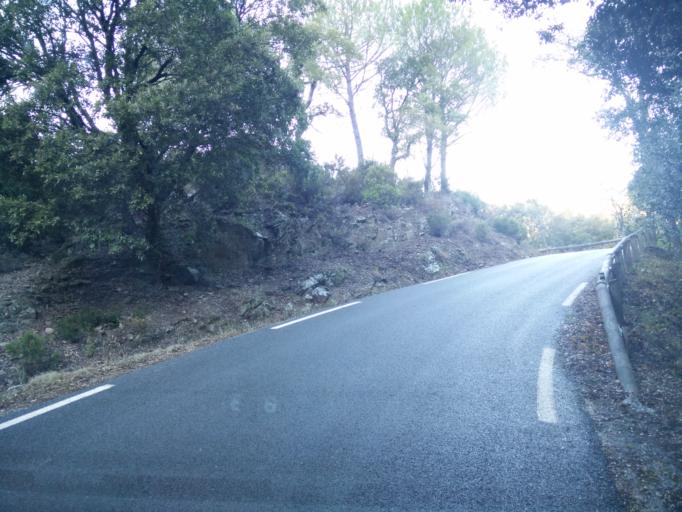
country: FR
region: Provence-Alpes-Cote d'Azur
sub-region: Departement du Var
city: Collobrieres
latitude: 43.2328
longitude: 6.3685
